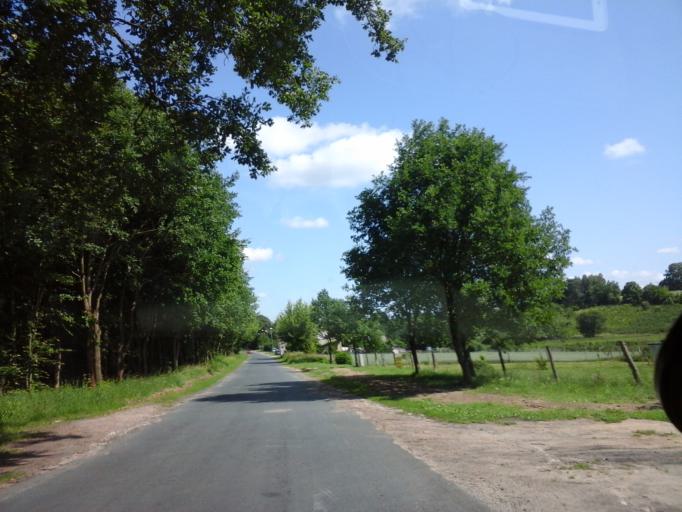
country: PL
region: West Pomeranian Voivodeship
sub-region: Powiat choszczenski
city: Recz
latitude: 53.2463
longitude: 15.5422
